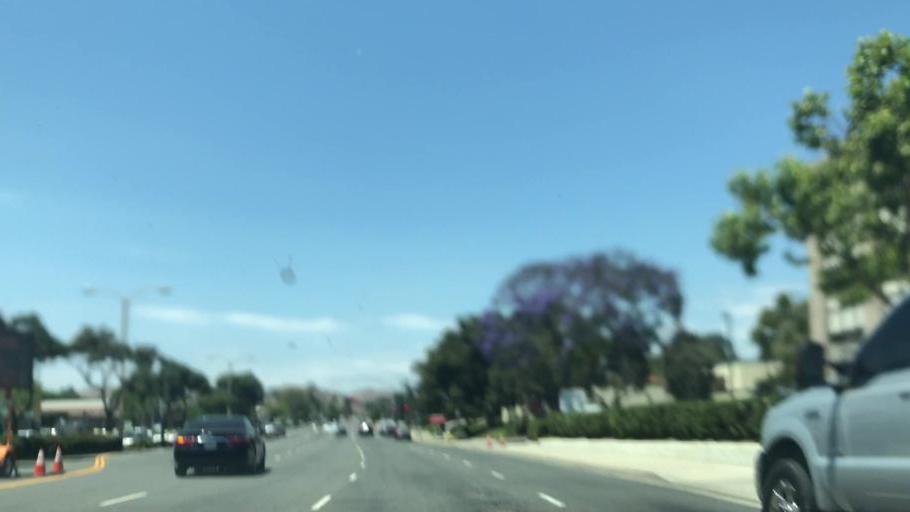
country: US
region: California
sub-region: Ventura County
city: El Rio
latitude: 34.2641
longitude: -119.2120
